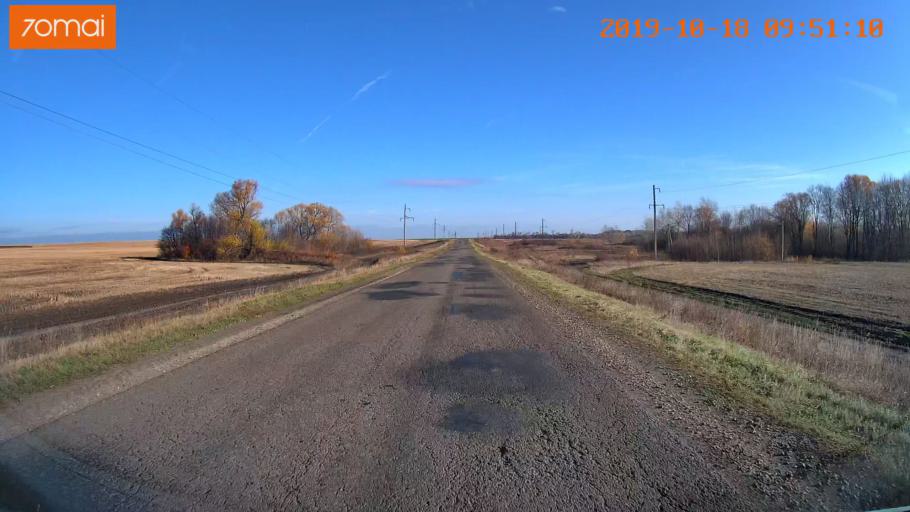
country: RU
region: Tula
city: Kazachka
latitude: 53.3372
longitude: 38.2882
